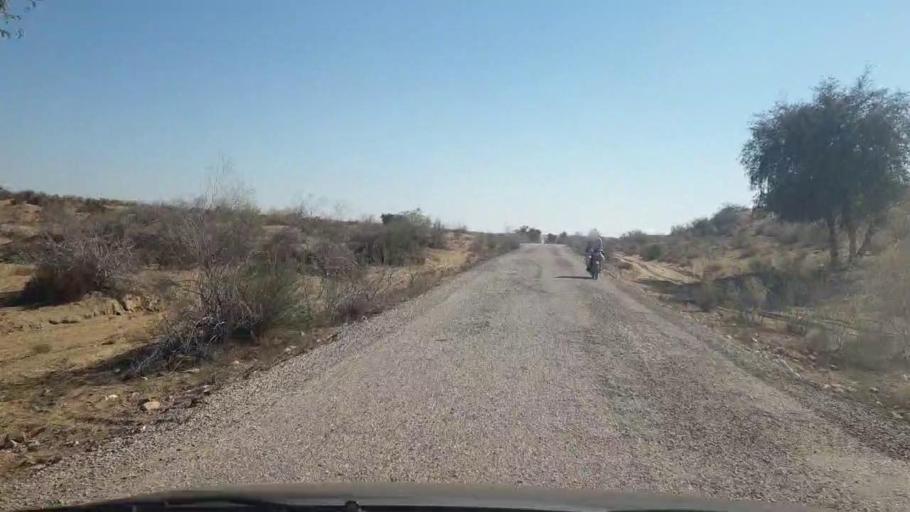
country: PK
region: Sindh
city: Bozdar
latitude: 27.0361
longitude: 68.6963
